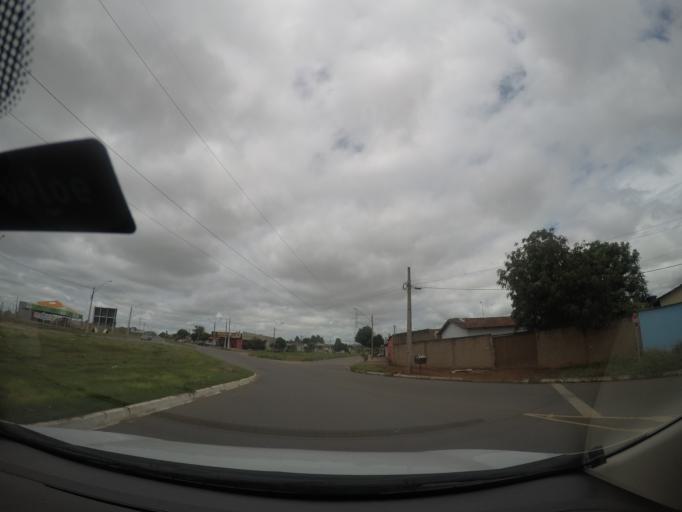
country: BR
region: Goias
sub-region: Goiania
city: Goiania
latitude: -16.7377
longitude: -49.3673
